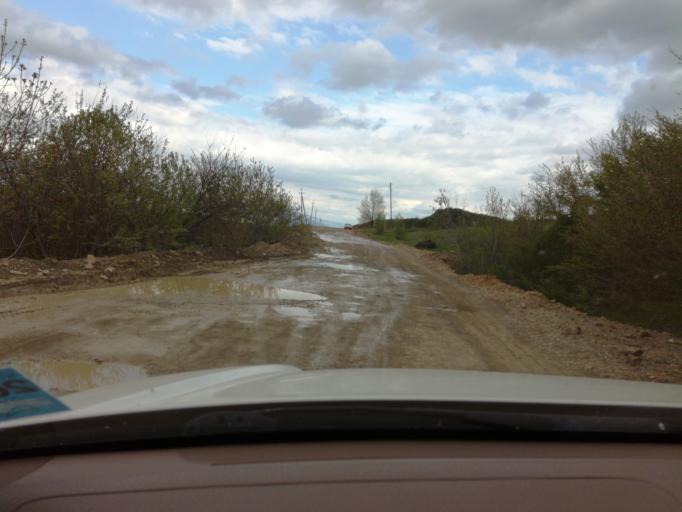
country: AM
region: Lorri
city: Urrut
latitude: 41.0150
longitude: 44.3087
